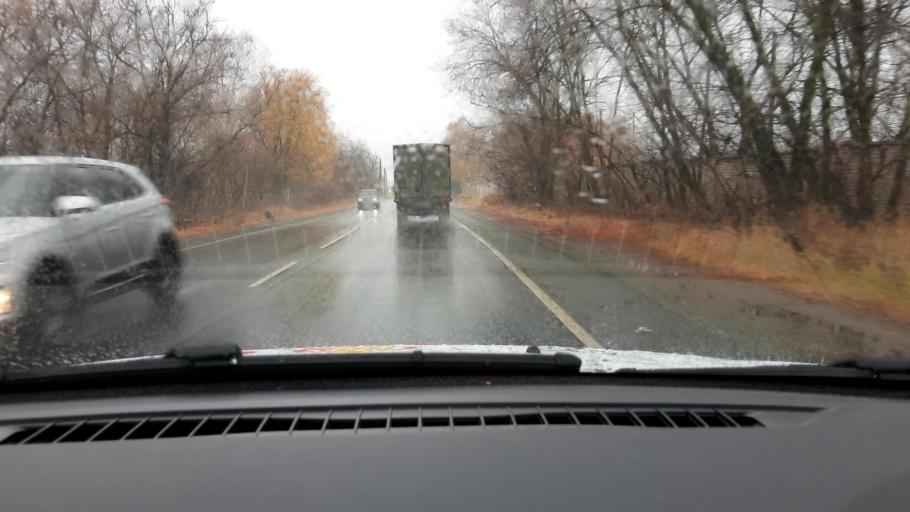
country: RU
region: Nizjnij Novgorod
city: Babino
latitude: 56.2586
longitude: 43.6437
